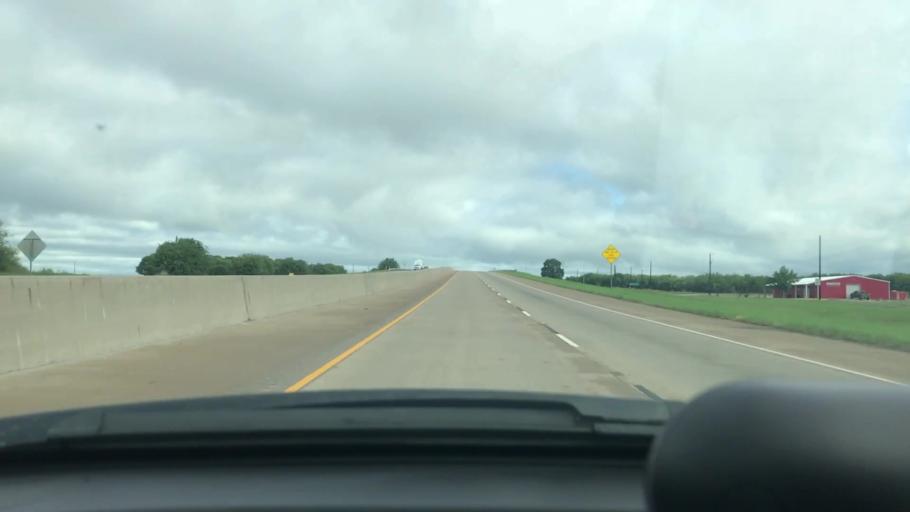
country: US
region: Texas
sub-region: Grayson County
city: Howe
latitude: 33.4621
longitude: -96.6110
